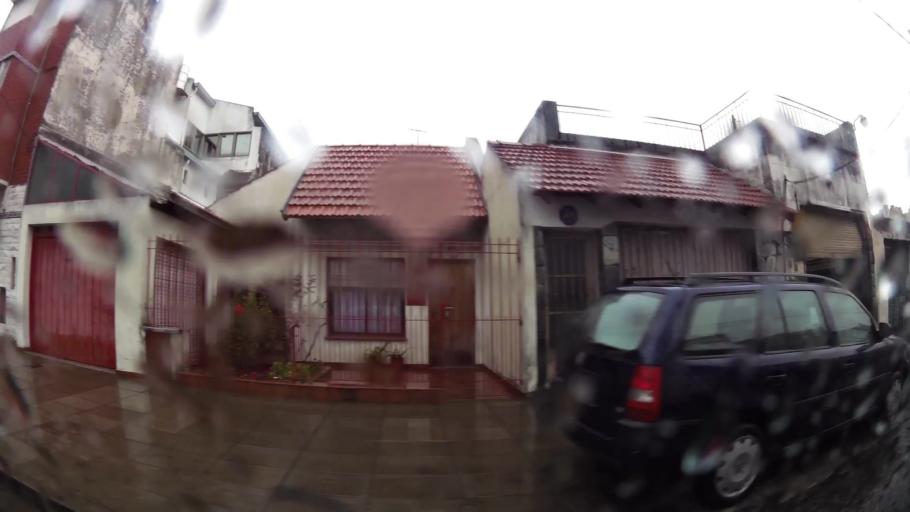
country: AR
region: Buenos Aires
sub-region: Partido de Lanus
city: Lanus
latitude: -34.7271
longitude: -58.4002
